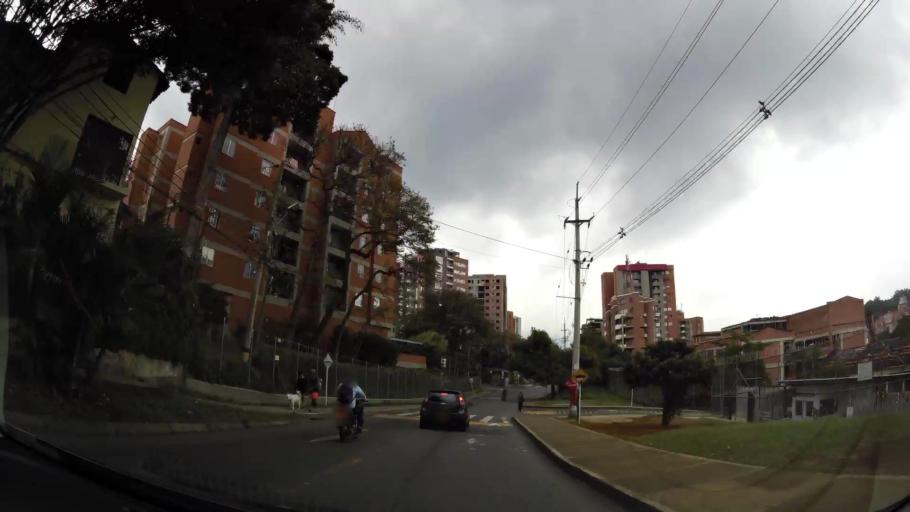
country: CO
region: Antioquia
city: Medellin
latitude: 6.2764
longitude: -75.5868
